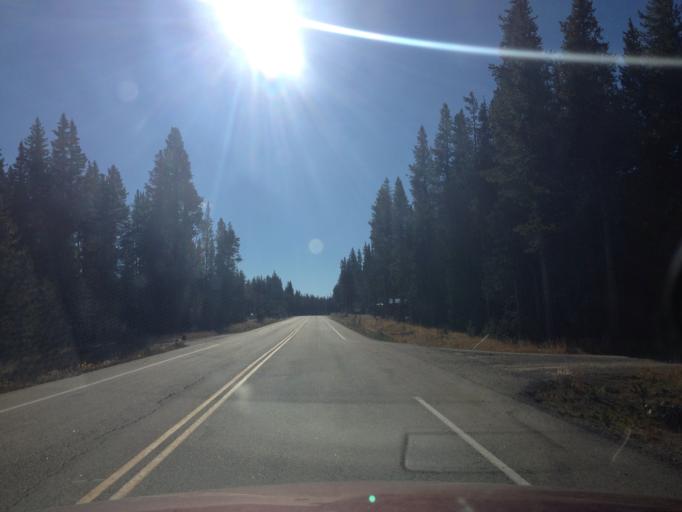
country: US
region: Montana
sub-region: Carbon County
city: Red Lodge
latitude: 45.0245
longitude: -109.8810
